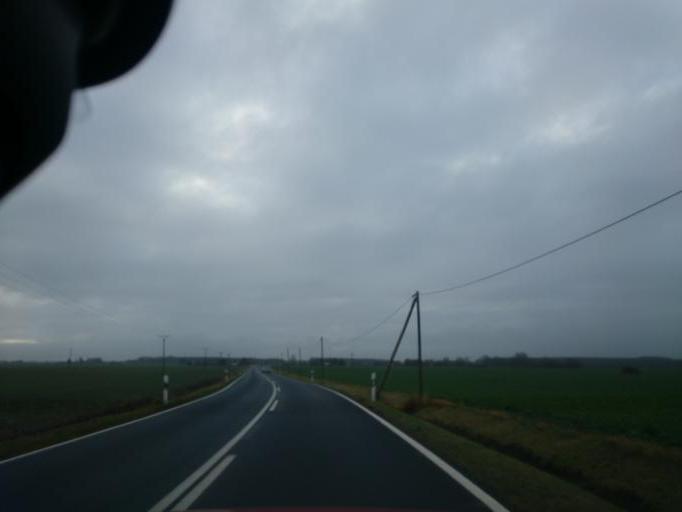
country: DE
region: Mecklenburg-Vorpommern
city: Trinwillershagen
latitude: 54.2940
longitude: 12.5843
